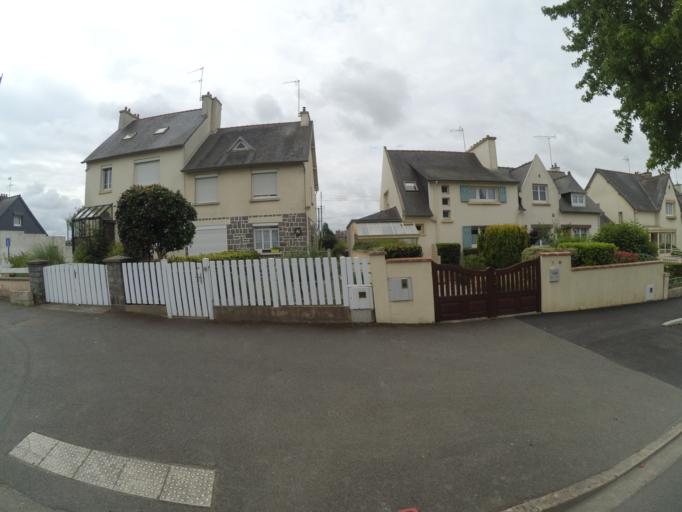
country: FR
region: Brittany
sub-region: Departement des Cotes-d'Armor
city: Saint-Brieuc
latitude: 48.5096
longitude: -2.7780
